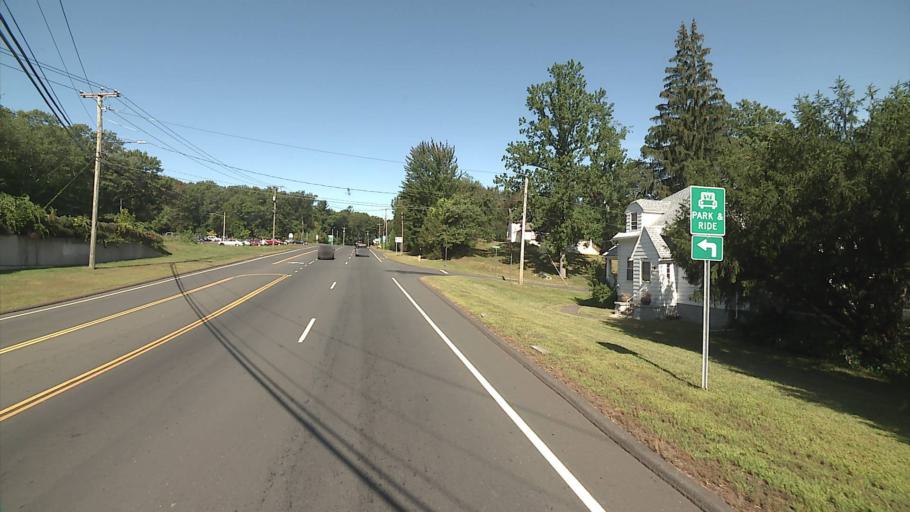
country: US
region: Connecticut
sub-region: New Haven County
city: Prospect
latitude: 41.5422
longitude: -72.9530
